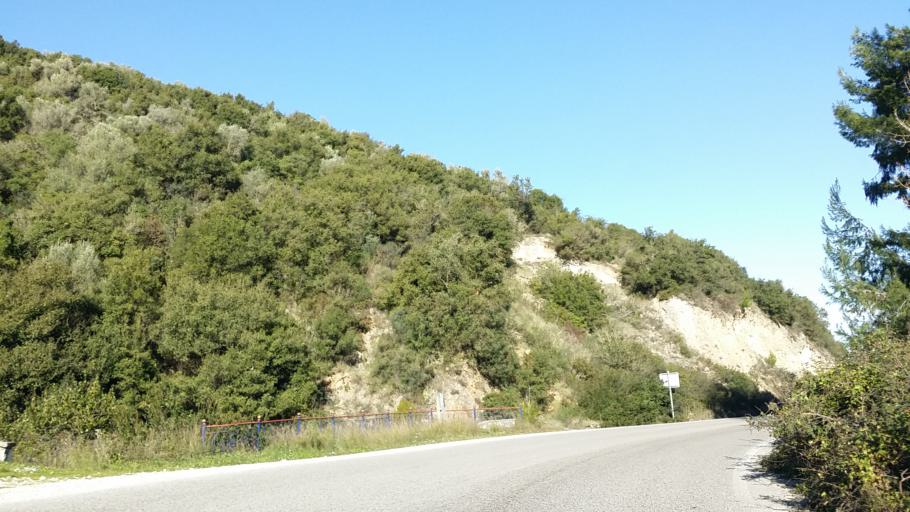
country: GR
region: West Greece
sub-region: Nomos Aitolias kai Akarnanias
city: Monastirakion
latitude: 38.9094
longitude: 20.9469
